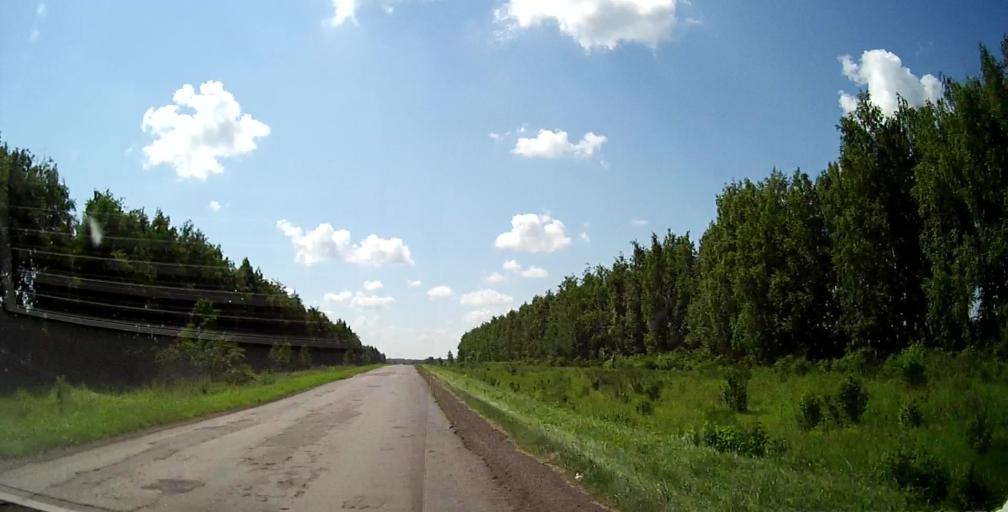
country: RU
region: Lipetsk
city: Chaplygin
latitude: 53.3626
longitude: 39.9196
